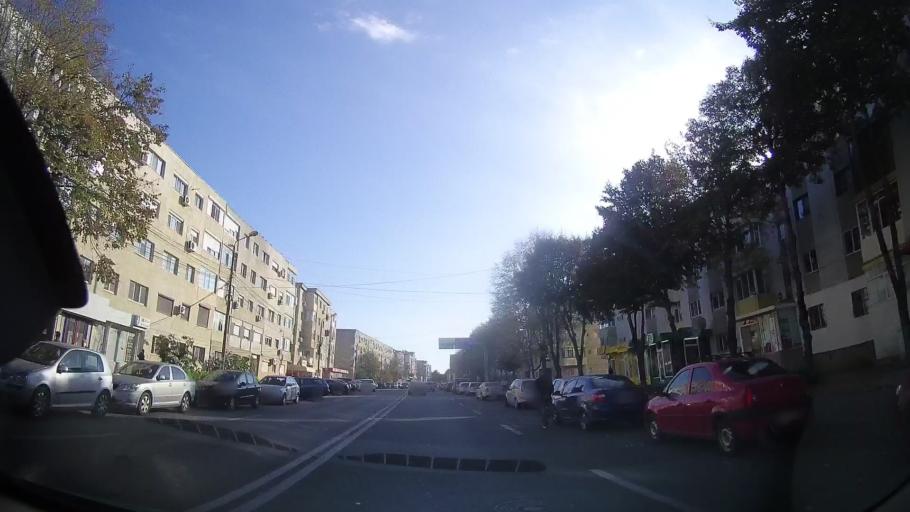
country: RO
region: Constanta
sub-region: Municipiul Mangalia
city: Mangalia
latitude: 43.8202
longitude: 28.5828
